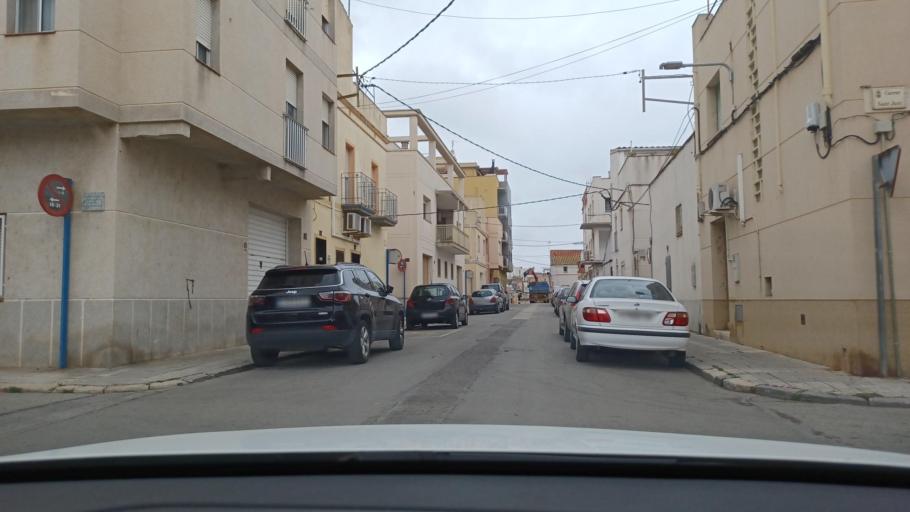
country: ES
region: Catalonia
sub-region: Provincia de Tarragona
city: Amposta
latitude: 40.7143
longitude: 0.5751
